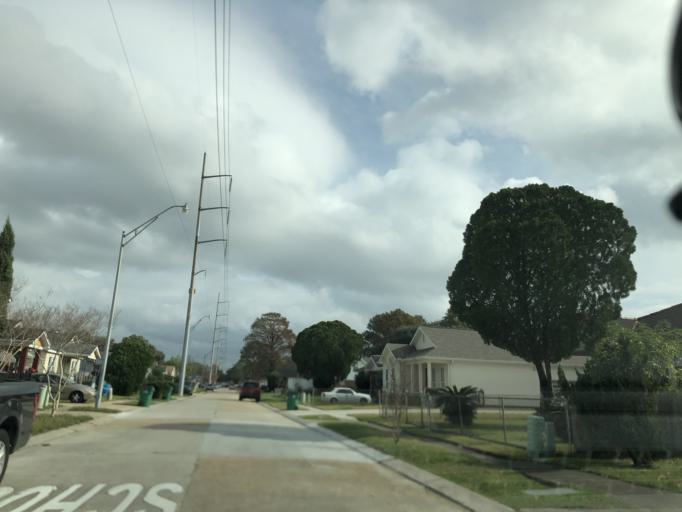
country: US
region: Louisiana
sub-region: Jefferson Parish
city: Metairie Terrace
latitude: 29.9769
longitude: -90.1691
